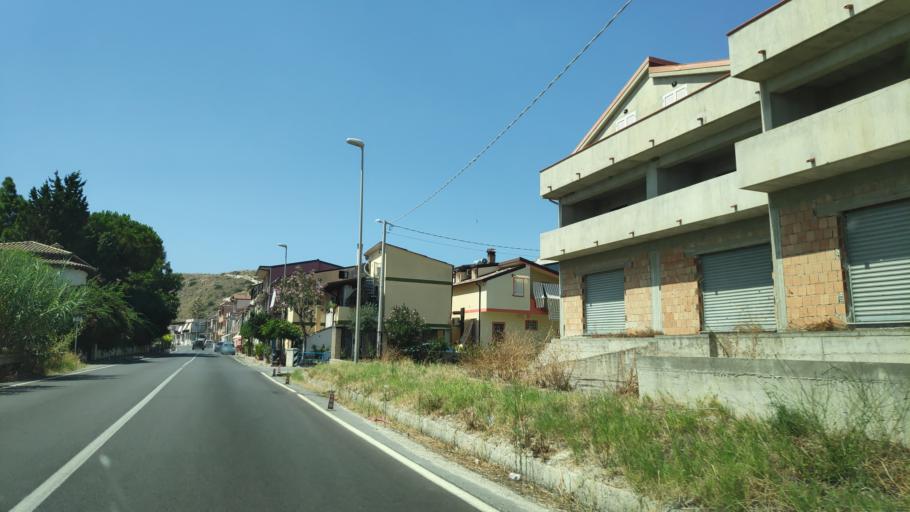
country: IT
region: Calabria
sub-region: Provincia di Reggio Calabria
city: Weather Station
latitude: 37.9328
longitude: 16.0693
